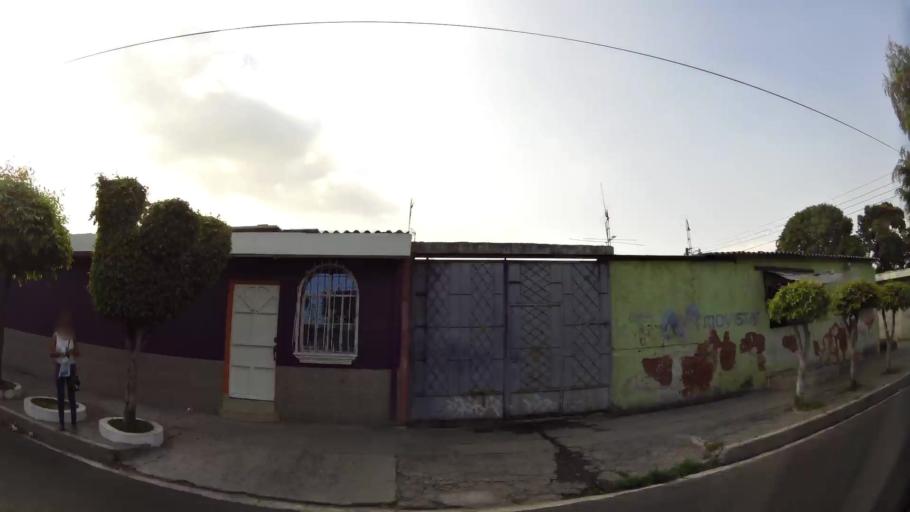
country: SV
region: San Salvador
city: Soyapango
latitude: 13.7253
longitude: -89.1271
